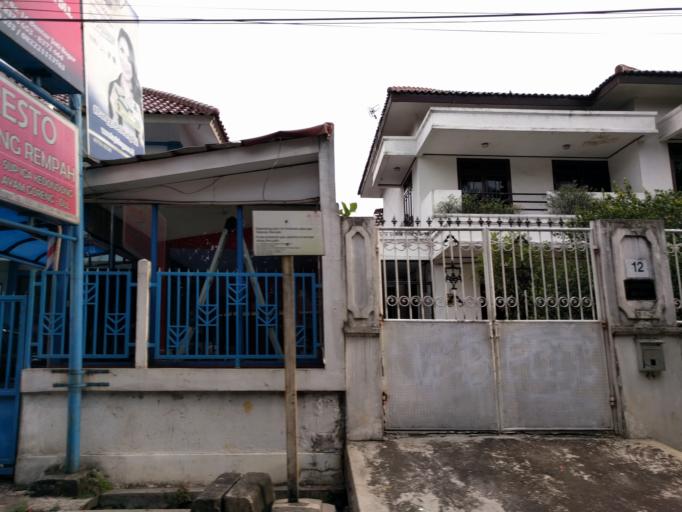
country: ID
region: West Java
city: Bogor
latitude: -6.5812
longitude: 106.8092
